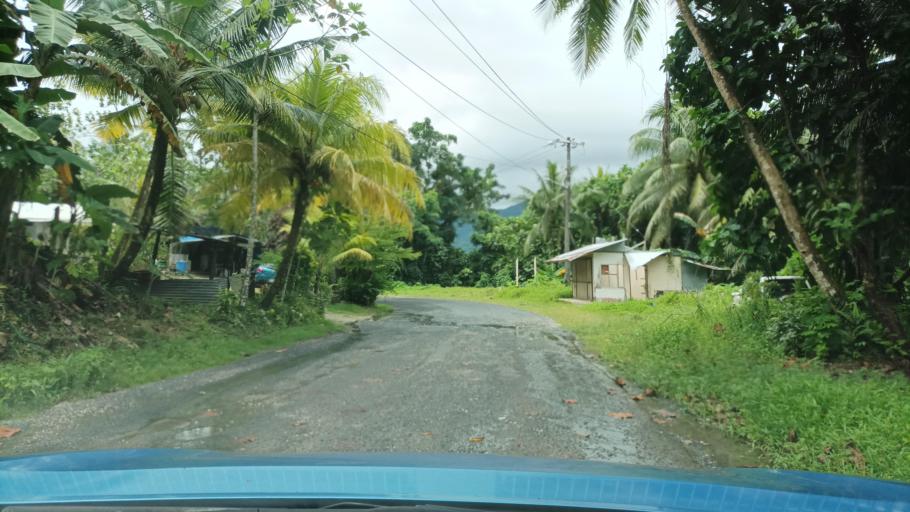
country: FM
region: Pohnpei
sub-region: Madolenihm Municipality
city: Madolenihm Municipality Government
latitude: 6.9201
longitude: 158.3084
